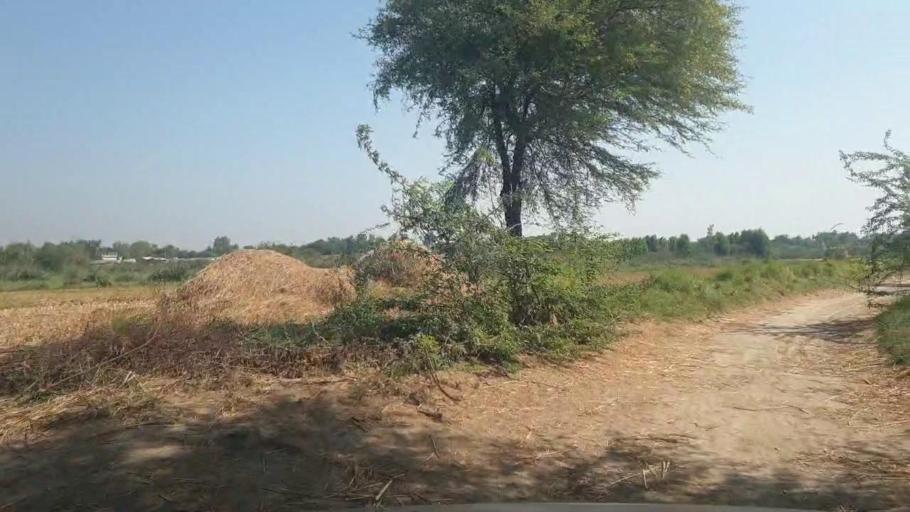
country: PK
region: Sindh
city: Badin
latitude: 24.6832
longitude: 68.8741
